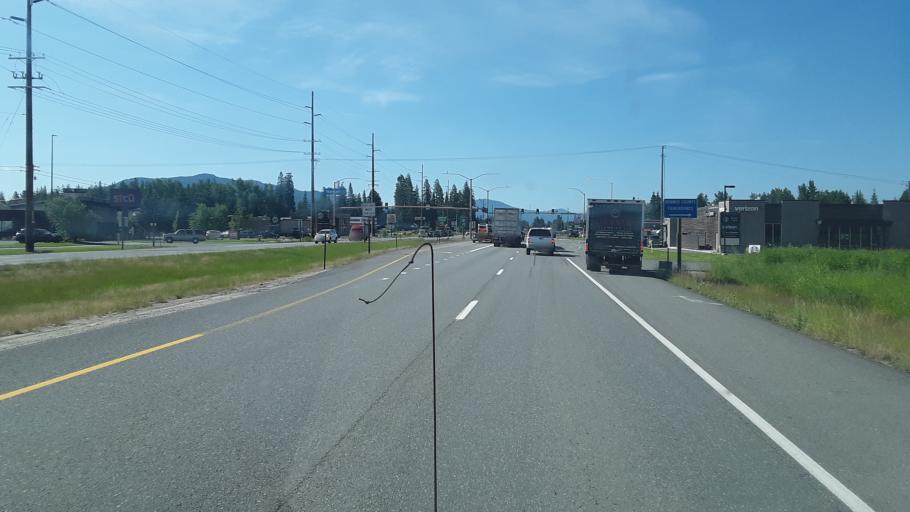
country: US
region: Idaho
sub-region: Bonner County
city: Ponderay
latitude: 48.3106
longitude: -116.5465
